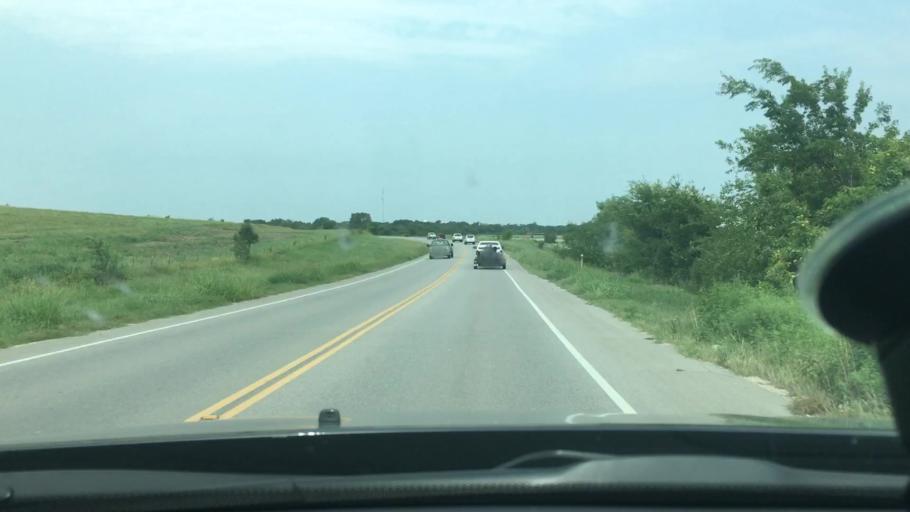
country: US
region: Oklahoma
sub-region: Marshall County
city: Madill
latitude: 34.0582
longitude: -96.7494
